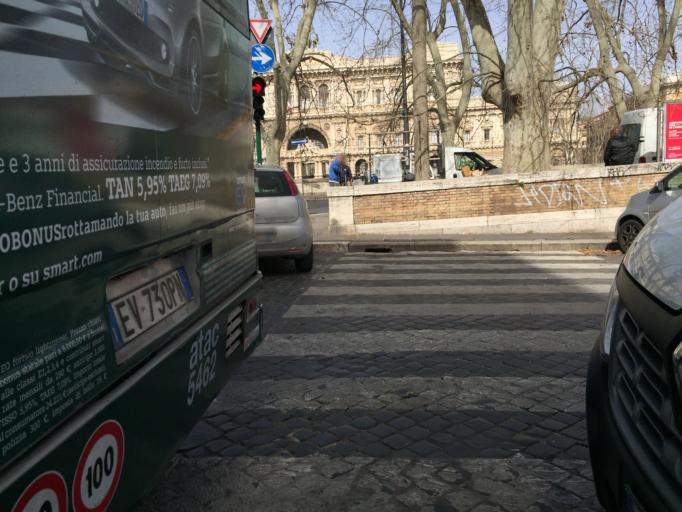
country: VA
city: Vatican City
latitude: 41.9022
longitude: 12.4722
